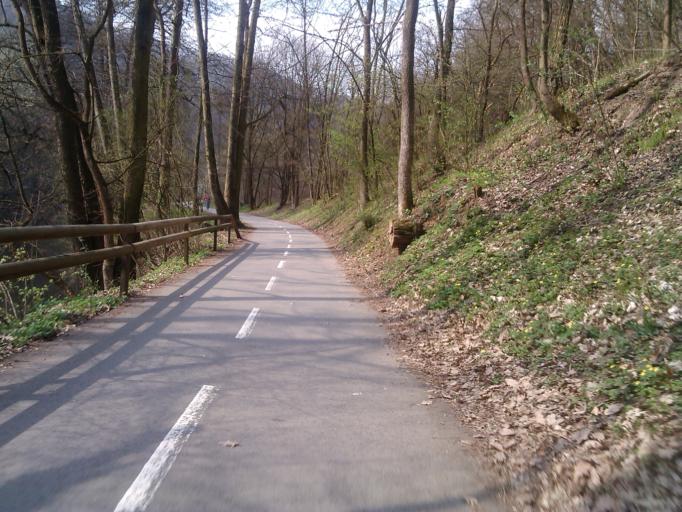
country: CZ
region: South Moravian
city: Bilovice nad Svitavou
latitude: 49.2343
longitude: 16.6727
